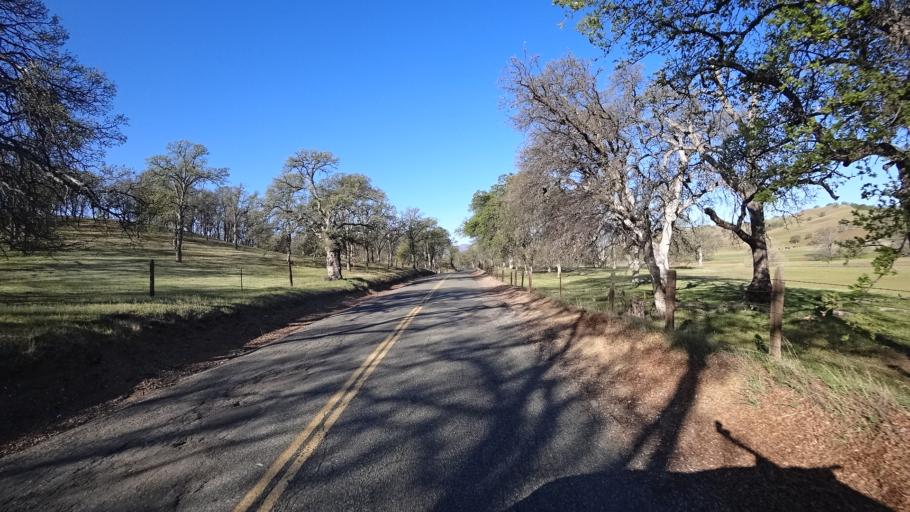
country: US
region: California
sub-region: Tehama County
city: Rancho Tehama Reserve
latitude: 39.7909
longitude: -122.4530
